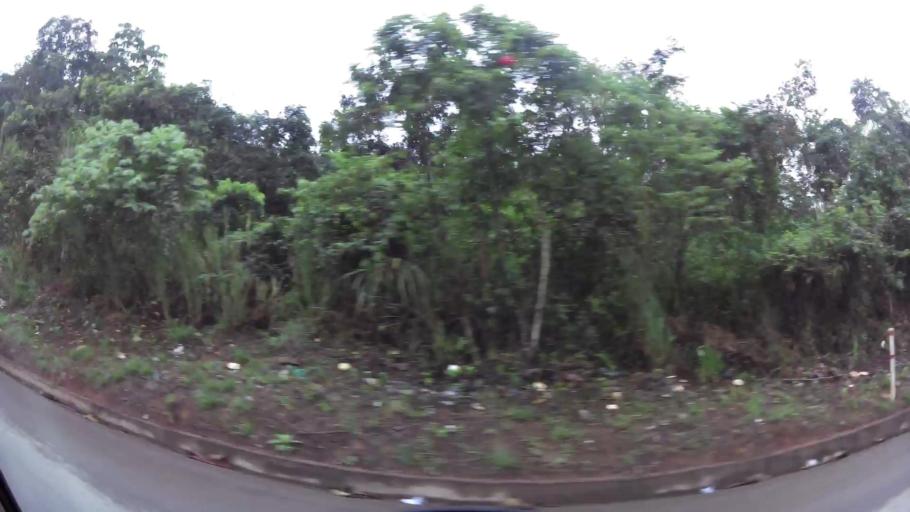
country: EC
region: El Oro
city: Pasaje
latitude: -3.3291
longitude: -79.7624
